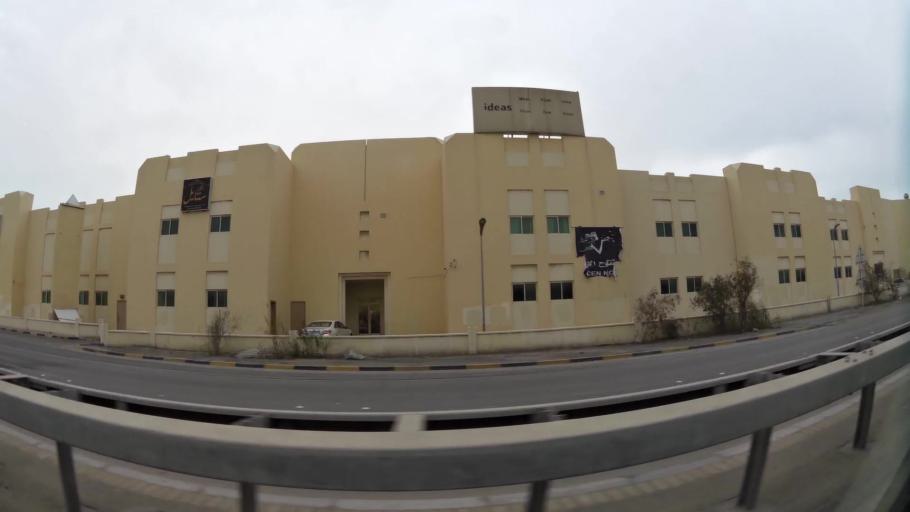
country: BH
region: Central Governorate
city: Madinat Hamad
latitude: 26.0941
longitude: 50.4883
